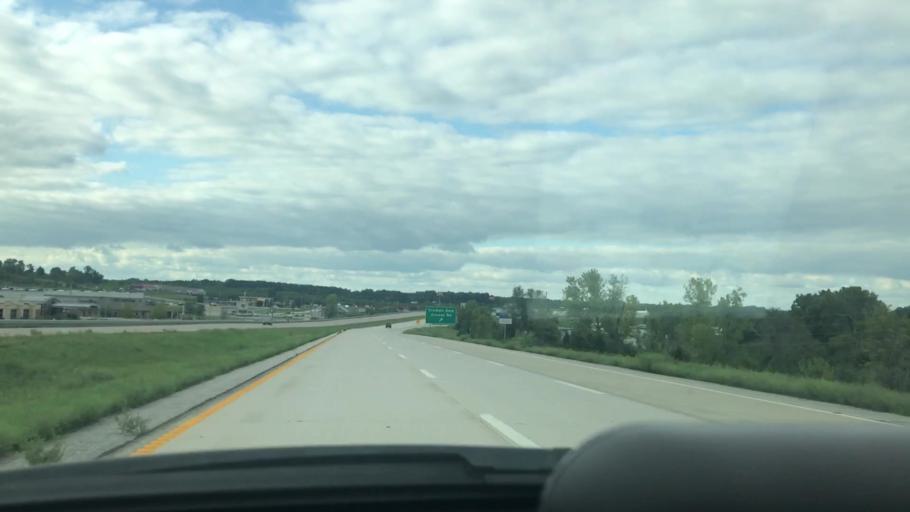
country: US
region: Missouri
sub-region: Benton County
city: Warsaw
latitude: 38.2579
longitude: -93.3666
